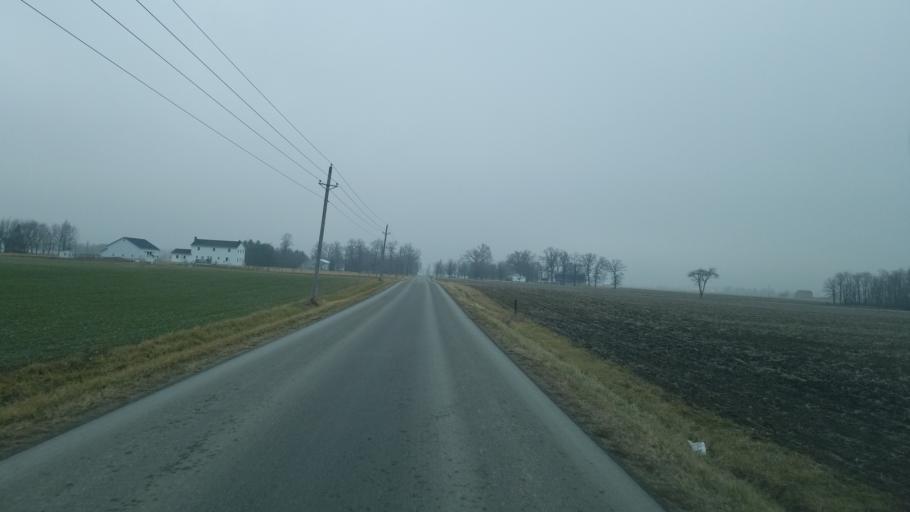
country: US
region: Indiana
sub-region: Adams County
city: Berne
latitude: 40.6814
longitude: -84.9943
